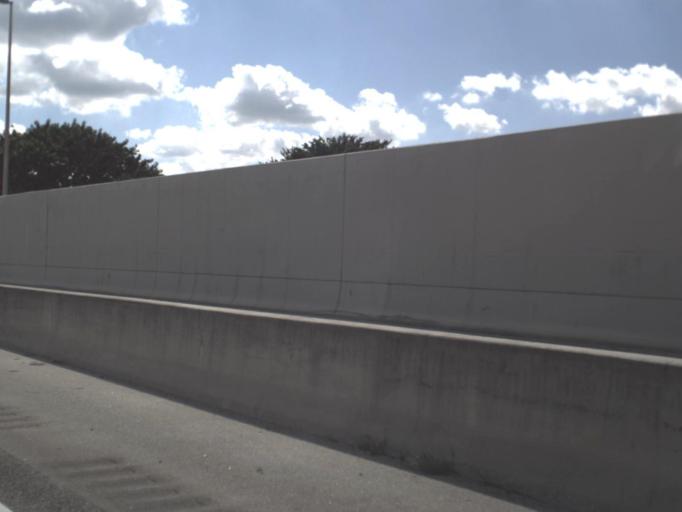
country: US
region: Florida
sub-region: Broward County
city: Lauderhill
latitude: 26.1344
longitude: -80.2190
